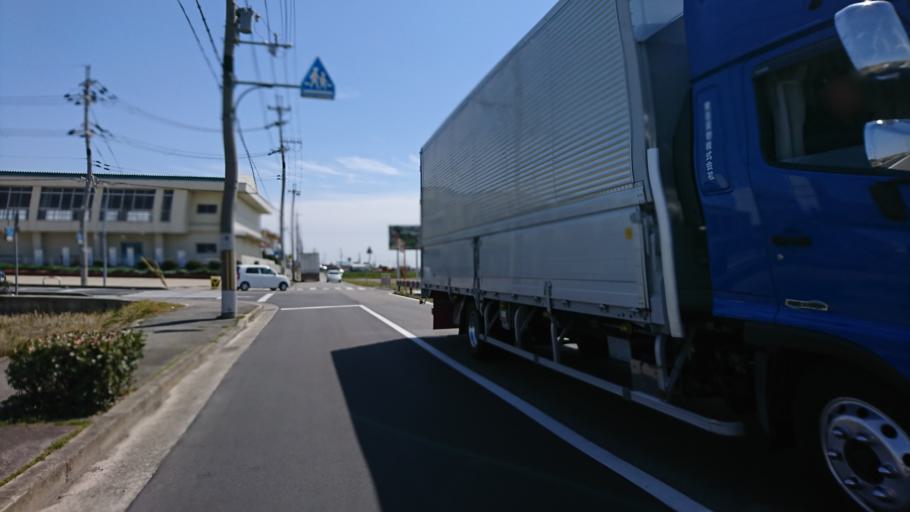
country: JP
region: Hyogo
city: Kakogawacho-honmachi
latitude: 34.7414
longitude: 134.8932
